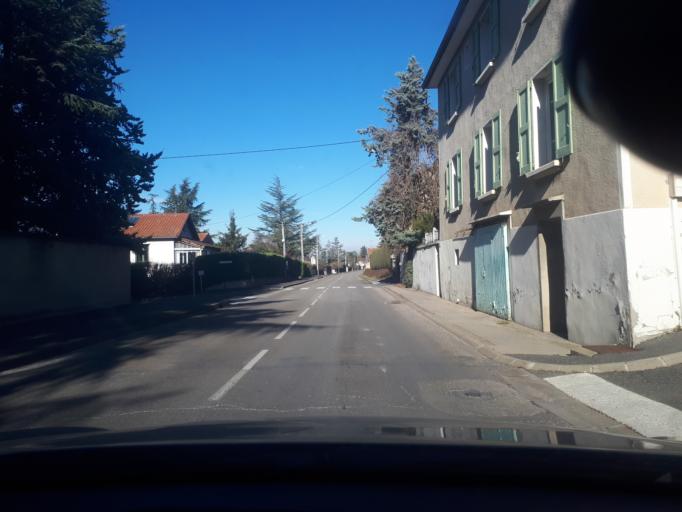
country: FR
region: Rhone-Alpes
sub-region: Departement de la Loire
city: Saint-Galmier
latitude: 45.6036
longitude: 4.3137
